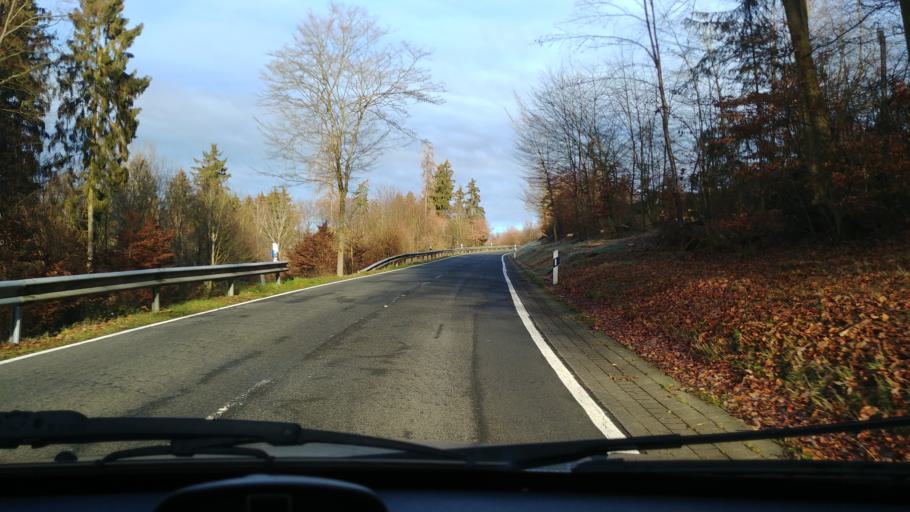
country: DE
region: Rheinland-Pfalz
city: Attenhausen
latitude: 50.2844
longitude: 7.8655
